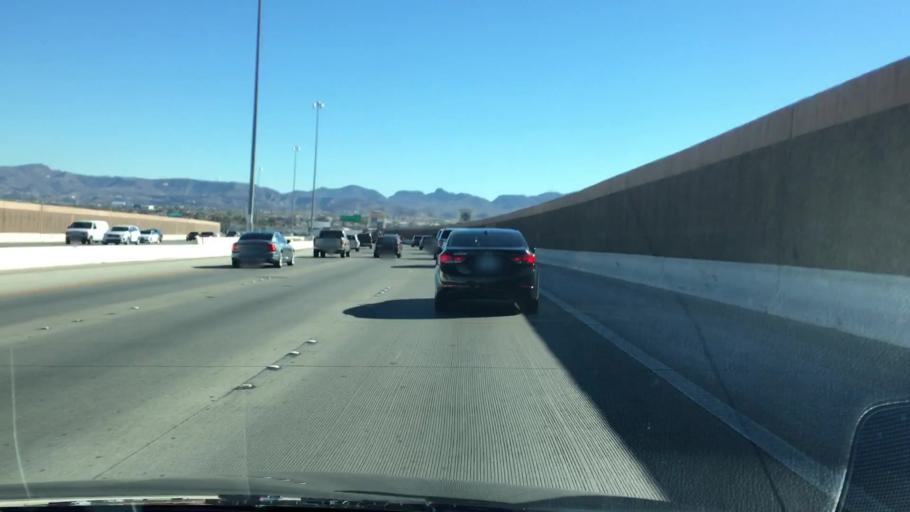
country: US
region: Nevada
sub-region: Clark County
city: Whitney
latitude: 36.0261
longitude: -115.1288
